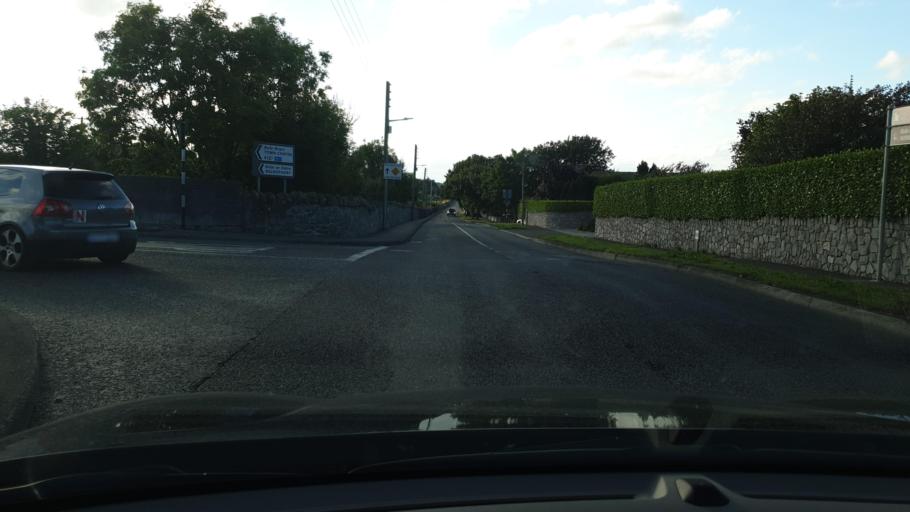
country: IE
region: Leinster
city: Balbriggan
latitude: 53.6060
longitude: -6.1722
